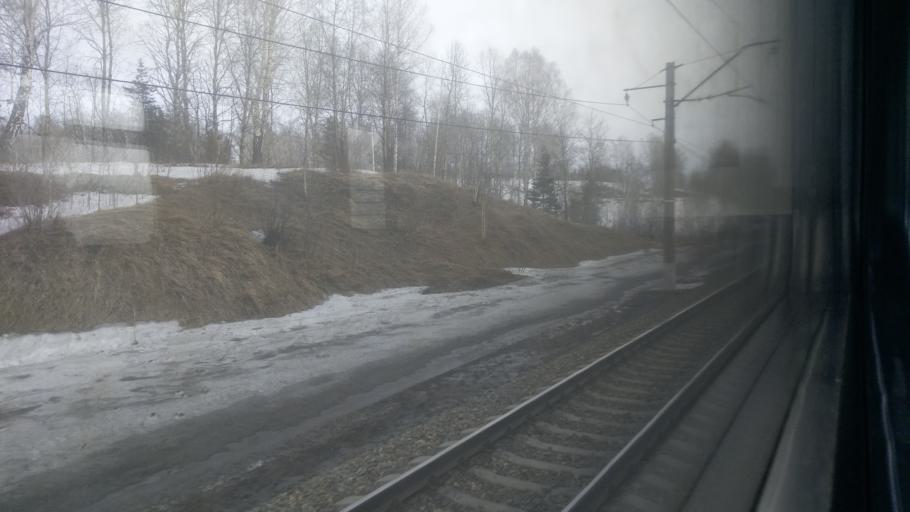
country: RU
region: Novosibirsk
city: Bolotnoye
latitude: 55.5967
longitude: 84.1412
